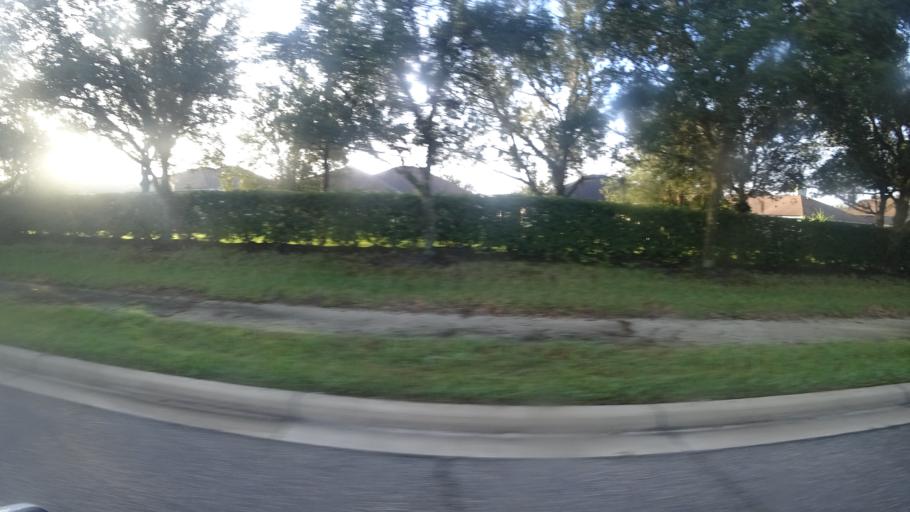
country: US
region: Florida
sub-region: Manatee County
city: Ellenton
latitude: 27.5353
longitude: -82.4246
